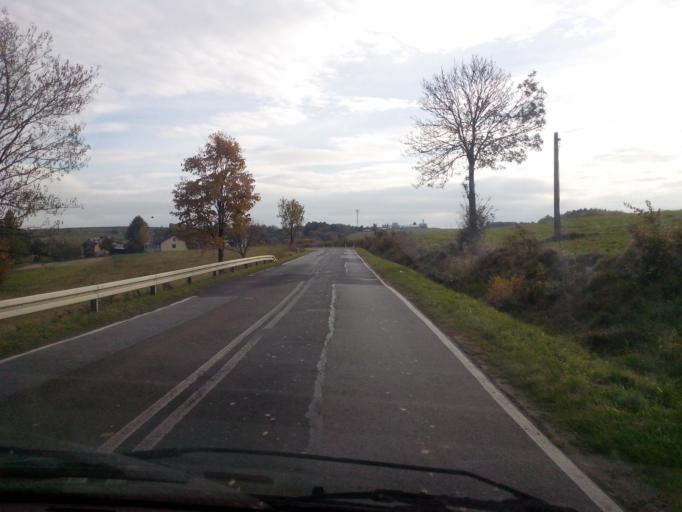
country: PL
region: Subcarpathian Voivodeship
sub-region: Powiat ropczycko-sedziszowski
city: Wielopole Skrzynskie
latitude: 49.9247
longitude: 21.6099
